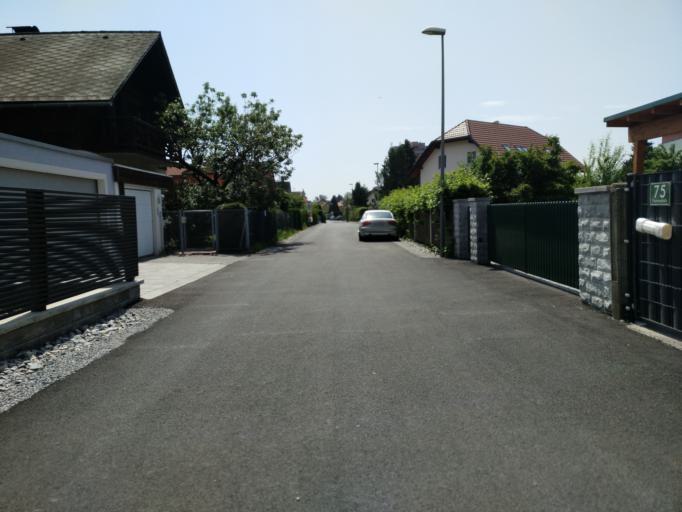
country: AT
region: Styria
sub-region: Graz Stadt
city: Goesting
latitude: 47.1011
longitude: 15.4063
